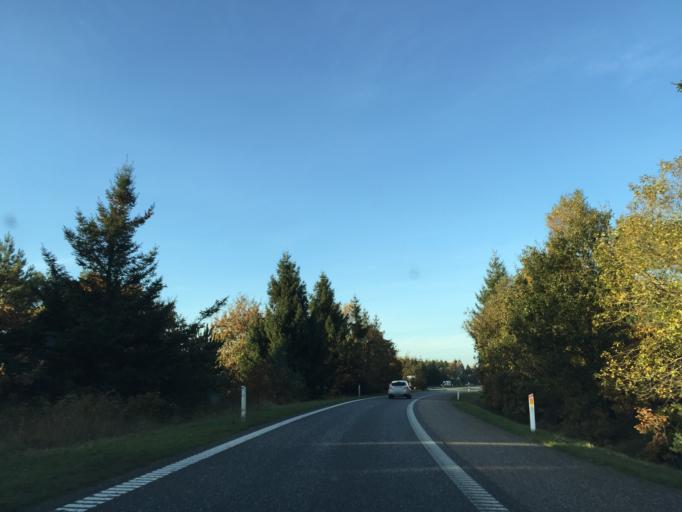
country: DK
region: South Denmark
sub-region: Aabenraa Kommune
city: Krusa
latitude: 54.8760
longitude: 9.3786
